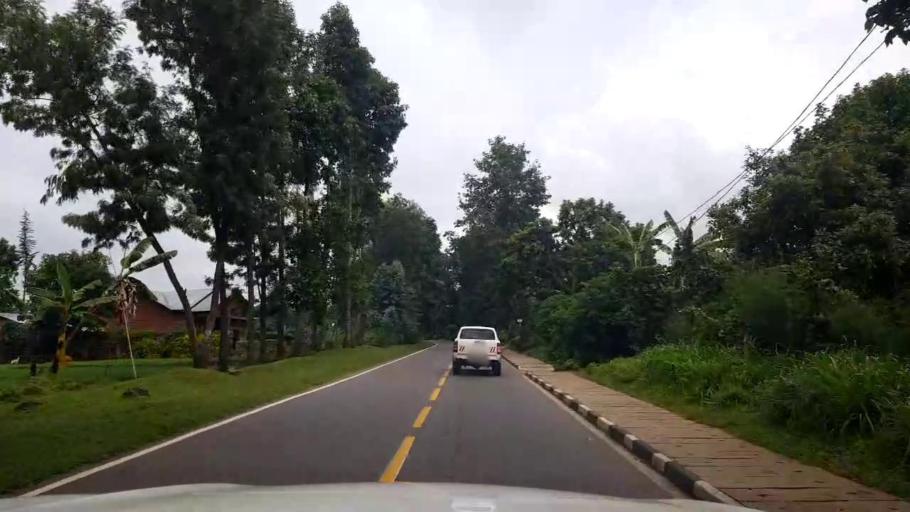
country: RW
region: Northern Province
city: Musanze
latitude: -1.4565
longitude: 29.6101
